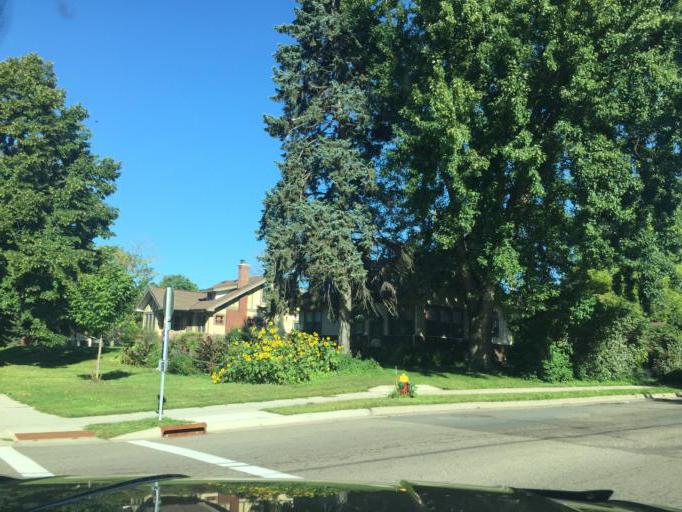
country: US
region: Minnesota
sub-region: Ramsey County
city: Little Canada
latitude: 44.9907
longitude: -93.0964
